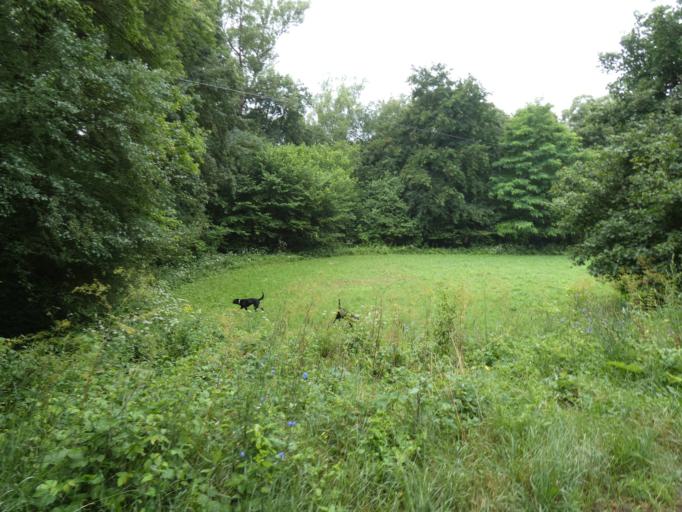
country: HU
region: Pest
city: Szob
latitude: 47.8154
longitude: 18.8993
